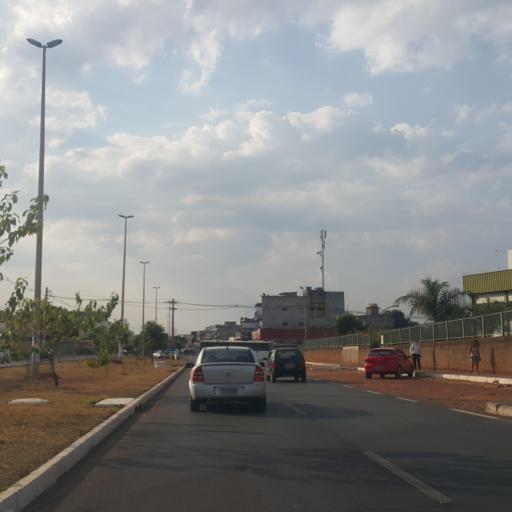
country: BR
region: Federal District
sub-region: Brasilia
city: Brasilia
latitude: -15.8670
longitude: -48.0232
